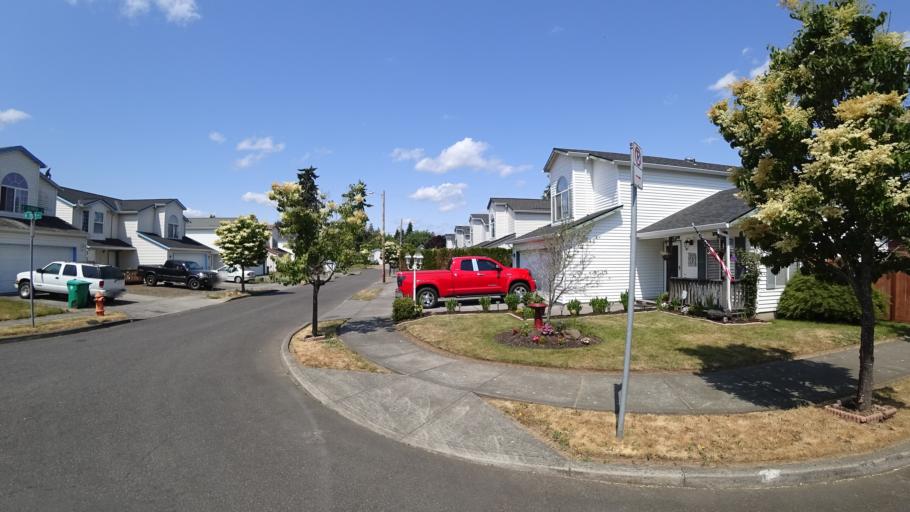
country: US
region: Oregon
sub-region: Washington County
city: West Haven
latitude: 45.5972
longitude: -122.7422
